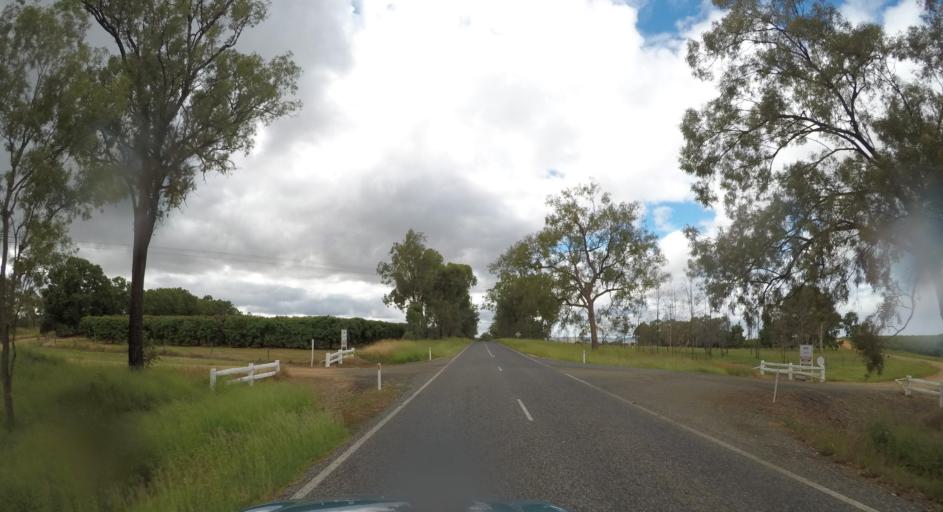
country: AU
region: Queensland
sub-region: North Burnett
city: Gayndah
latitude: -25.6279
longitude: 151.2849
